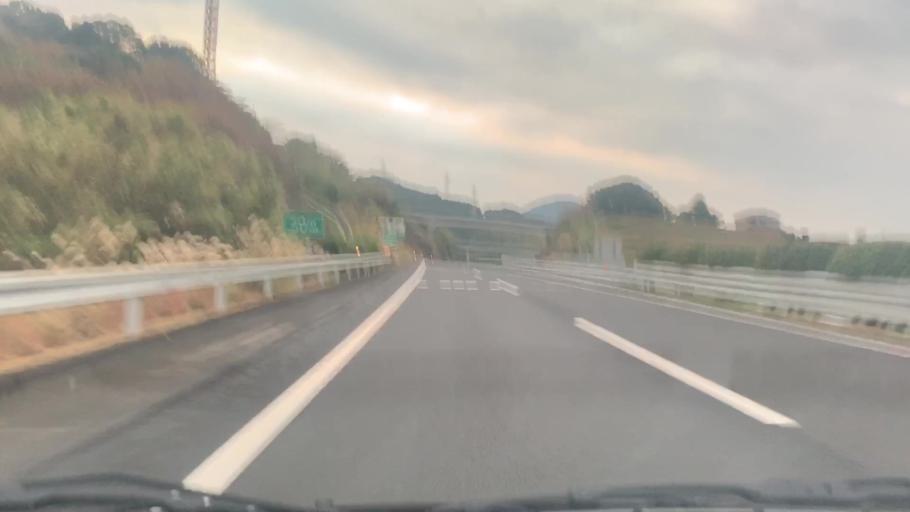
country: JP
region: Nagasaki
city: Omura
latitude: 33.0110
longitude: 129.9519
